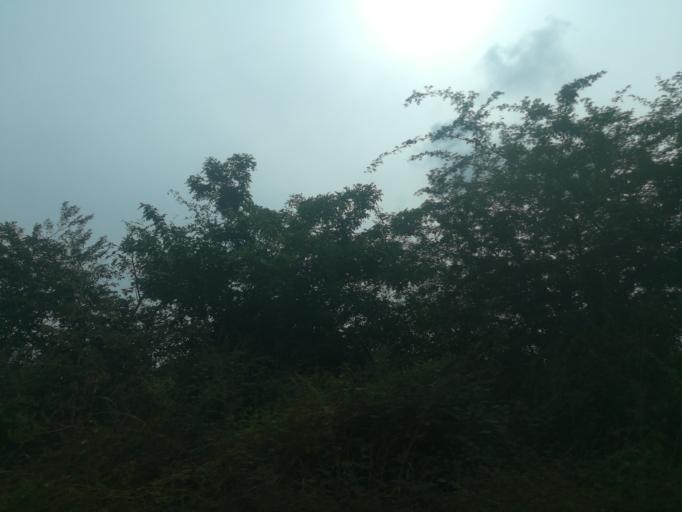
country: NG
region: Ogun
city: Ayetoro
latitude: 7.2898
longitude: 3.0817
